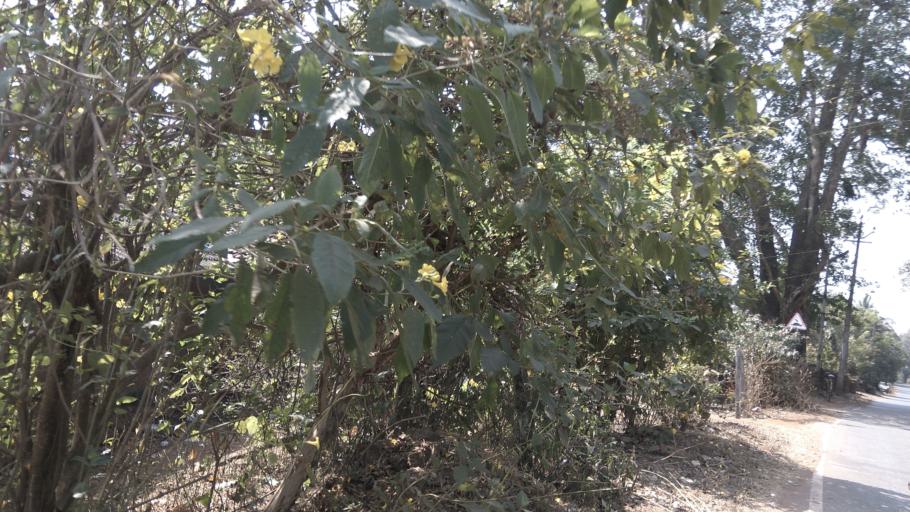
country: IN
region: Goa
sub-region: South Goa
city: Sanvordem
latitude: 15.3477
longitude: 74.2379
